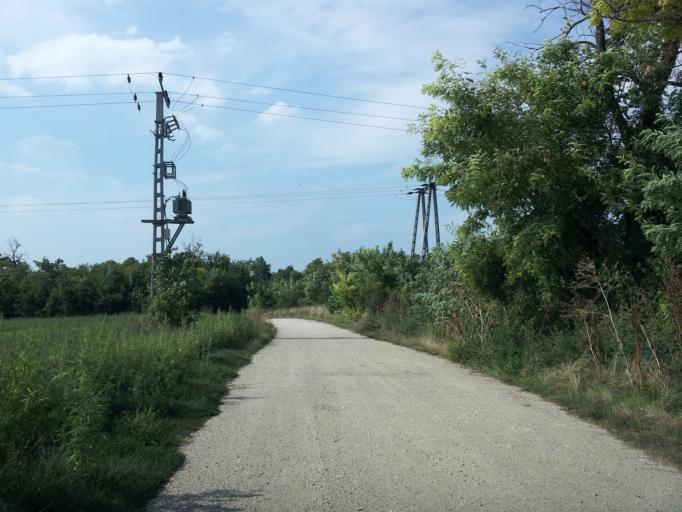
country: HU
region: Somogy
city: Balatonszabadi
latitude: 46.9416
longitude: 18.1655
